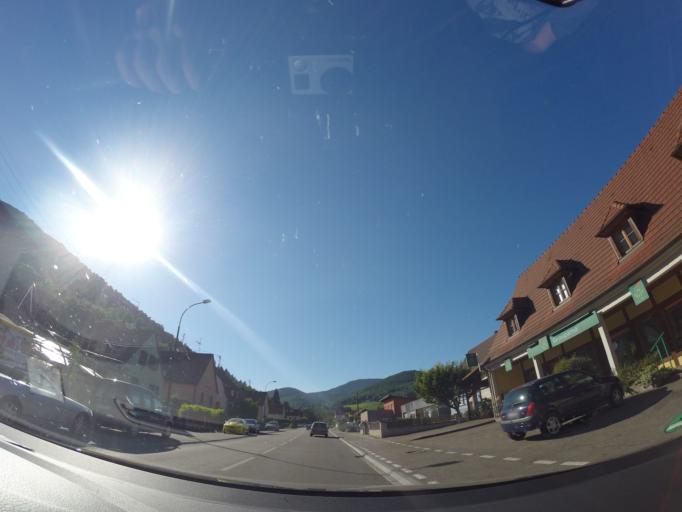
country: FR
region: Alsace
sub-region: Departement du Haut-Rhin
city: Kaysersberg
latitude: 48.1479
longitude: 7.2510
